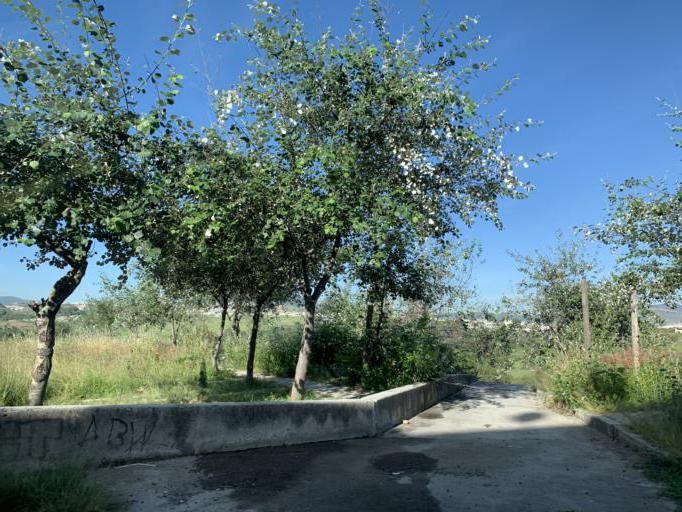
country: MX
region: Puebla
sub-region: Puebla
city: El Capulo (La Quebradora)
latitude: 18.9531
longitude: -98.2538
